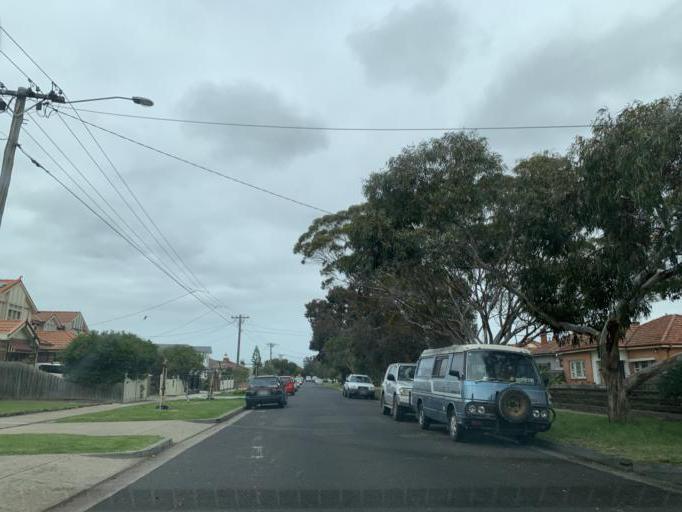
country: AU
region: Victoria
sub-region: Moreland
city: Pascoe Vale South
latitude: -37.7446
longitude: 144.9527
